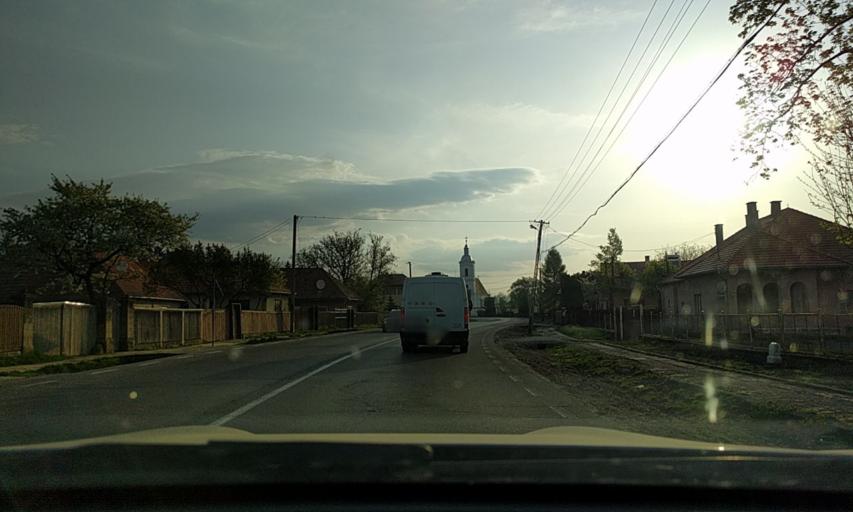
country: RO
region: Covasna
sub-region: Municipiul Targu Secuiesc
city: Lunga
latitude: 46.0224
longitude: 26.2180
